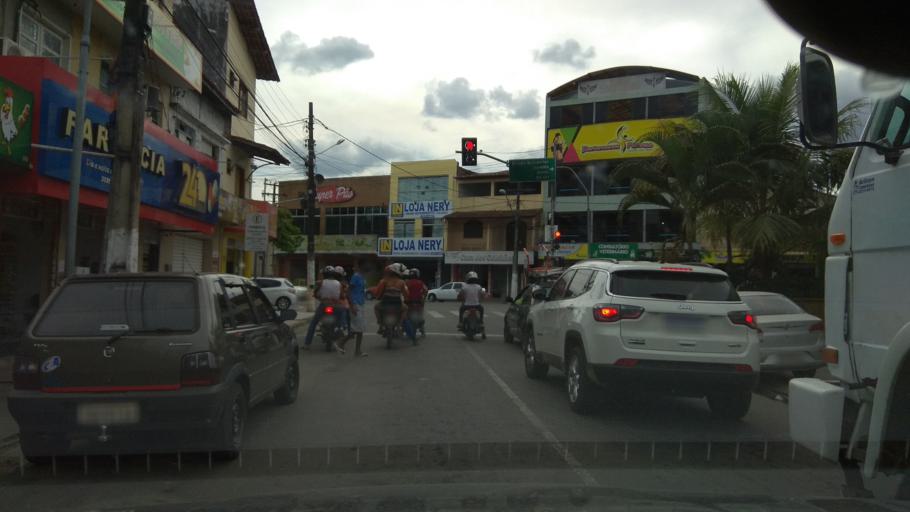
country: BR
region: Bahia
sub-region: Ipiau
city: Ipiau
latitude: -14.1351
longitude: -39.7384
